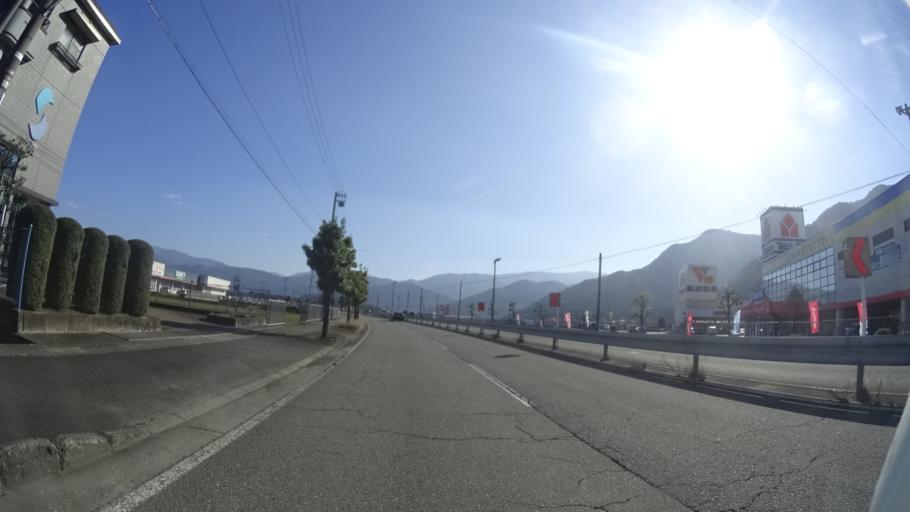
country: JP
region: Fukui
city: Ono
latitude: 35.9746
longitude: 136.4804
